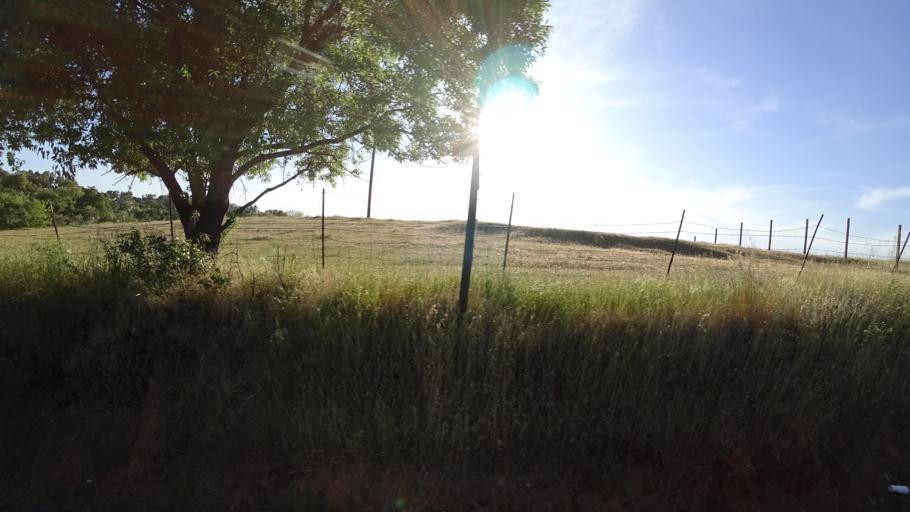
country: US
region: California
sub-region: Placer County
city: Lincoln
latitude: 38.9248
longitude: -121.2283
